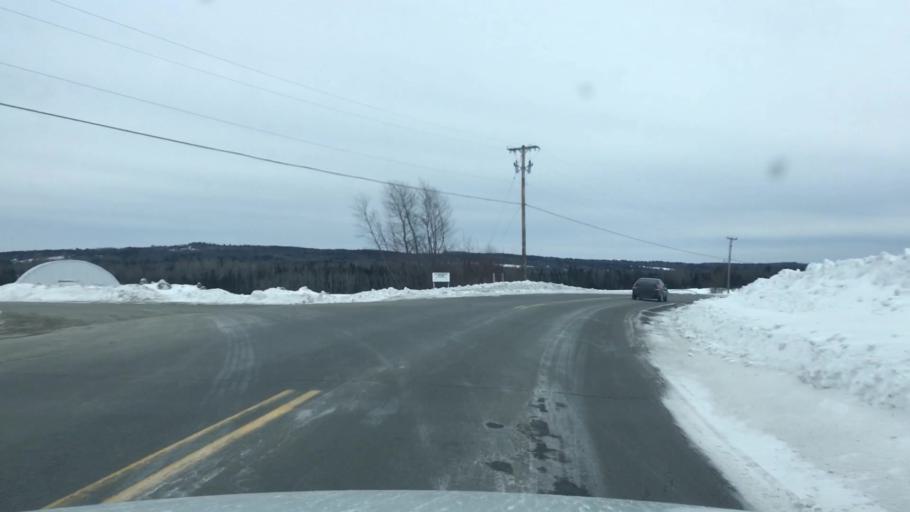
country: US
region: Maine
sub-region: Penobscot County
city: Garland
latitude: 44.9767
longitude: -69.0907
